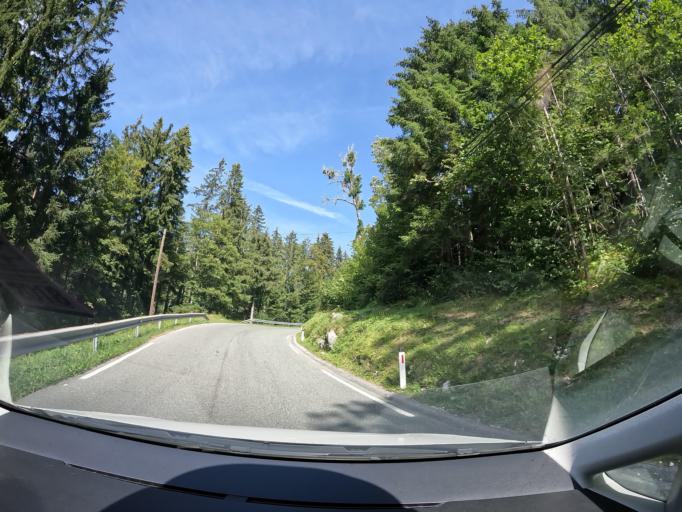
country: AT
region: Carinthia
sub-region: Politischer Bezirk Klagenfurt Land
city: Schiefling am See
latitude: 46.6112
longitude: 14.1111
